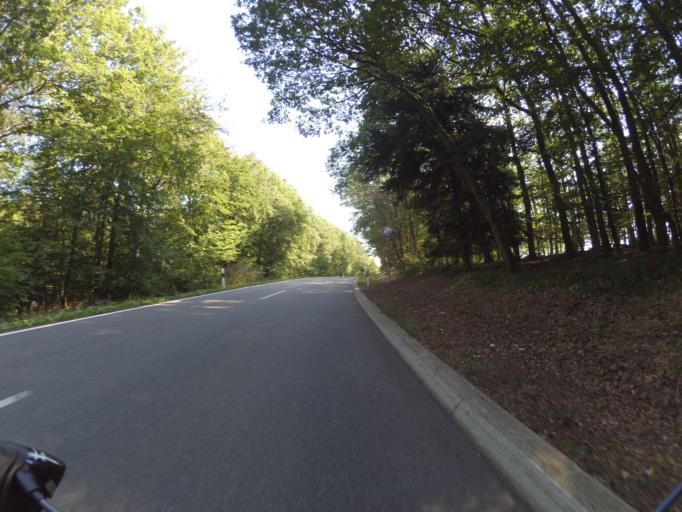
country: DE
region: Rheinland-Pfalz
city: Wintrich
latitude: 49.8609
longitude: 6.9744
